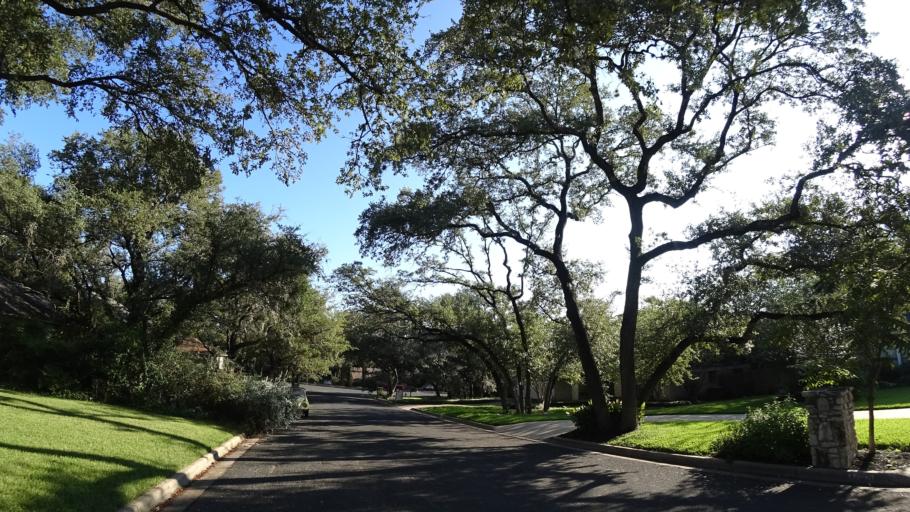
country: US
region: Texas
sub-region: Travis County
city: Rollingwood
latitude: 30.2659
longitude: -97.8059
